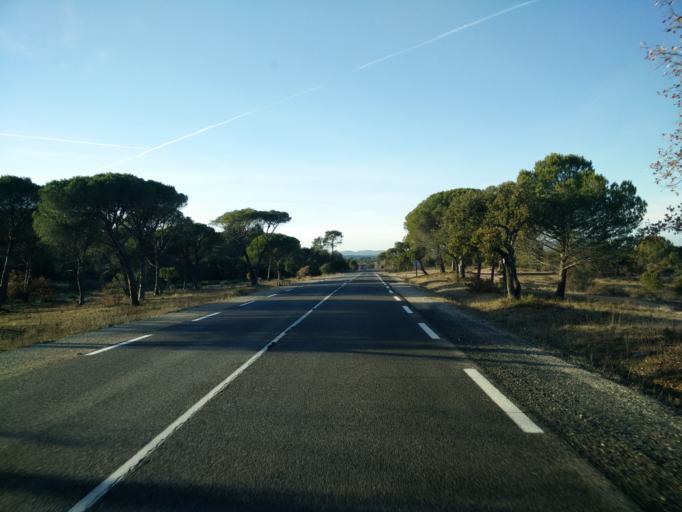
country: FR
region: Provence-Alpes-Cote d'Azur
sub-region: Departement du Var
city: La Garde-Freinet
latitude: 43.3512
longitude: 6.4231
